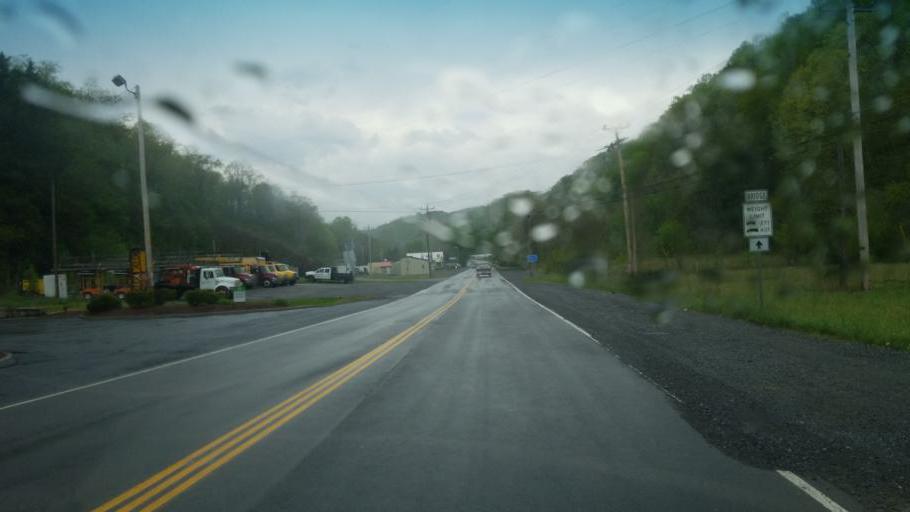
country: US
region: Virginia
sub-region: Smyth County
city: Marion
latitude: 36.8256
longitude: -81.5044
